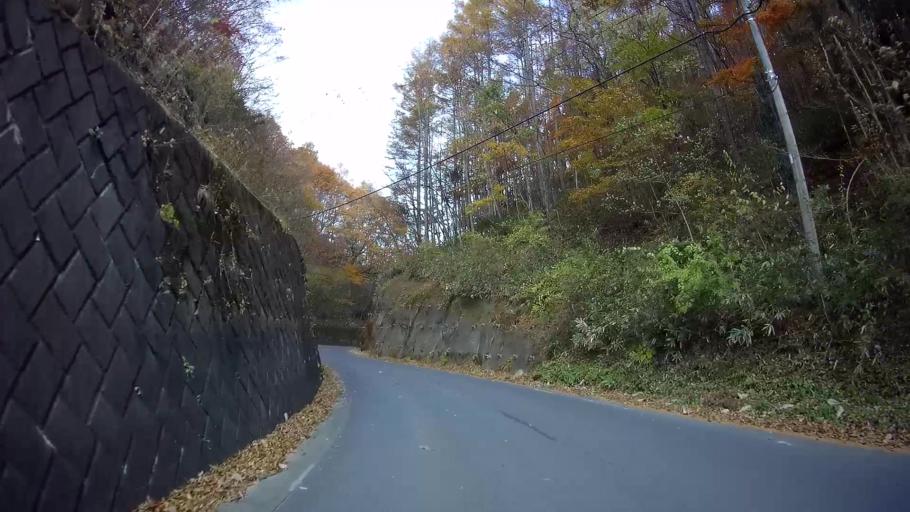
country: JP
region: Gunma
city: Nakanojomachi
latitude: 36.6319
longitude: 138.6364
